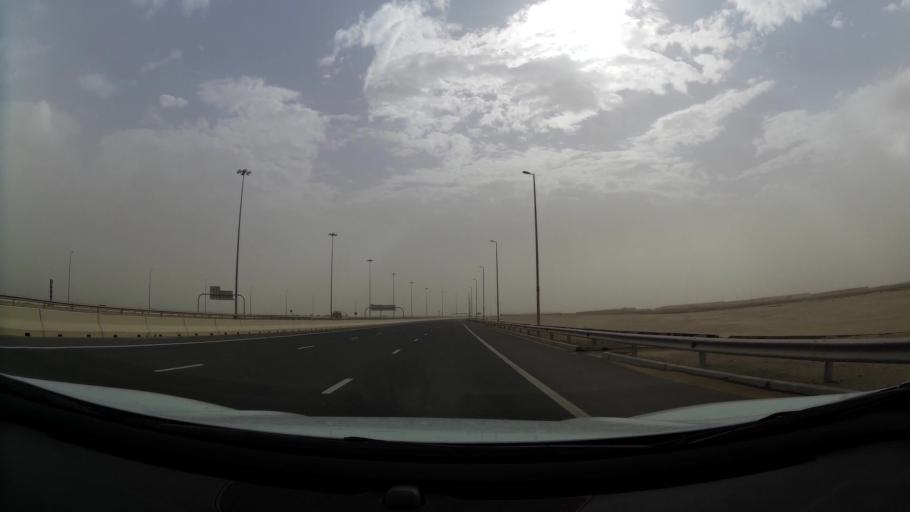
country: AE
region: Abu Dhabi
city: Abu Dhabi
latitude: 24.4820
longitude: 54.6540
